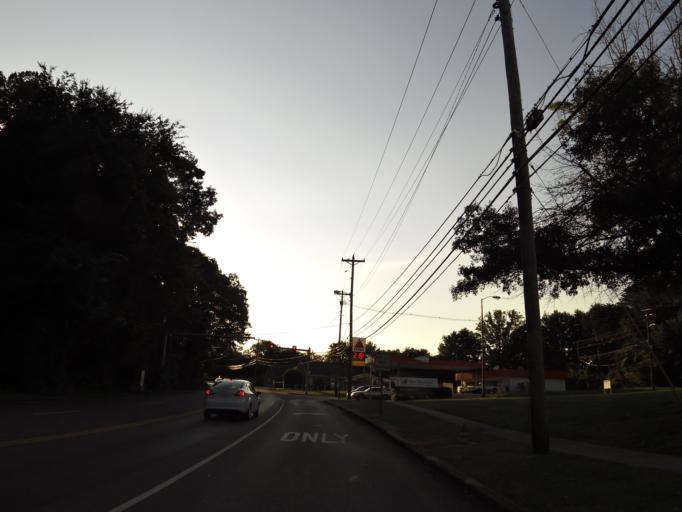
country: US
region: Tennessee
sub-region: McMinn County
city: Athens
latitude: 35.4406
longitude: -84.6082
